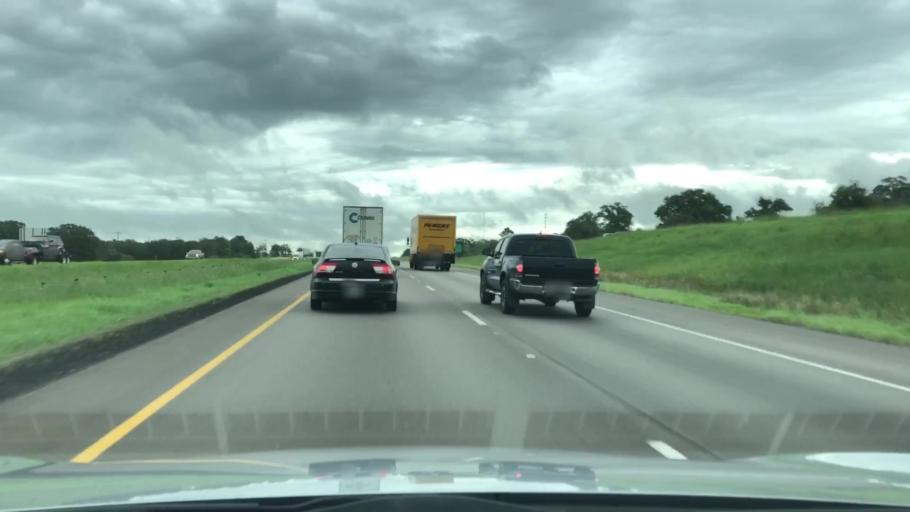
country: US
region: Texas
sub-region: Caldwell County
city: Luling
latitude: 29.6541
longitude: -97.5780
